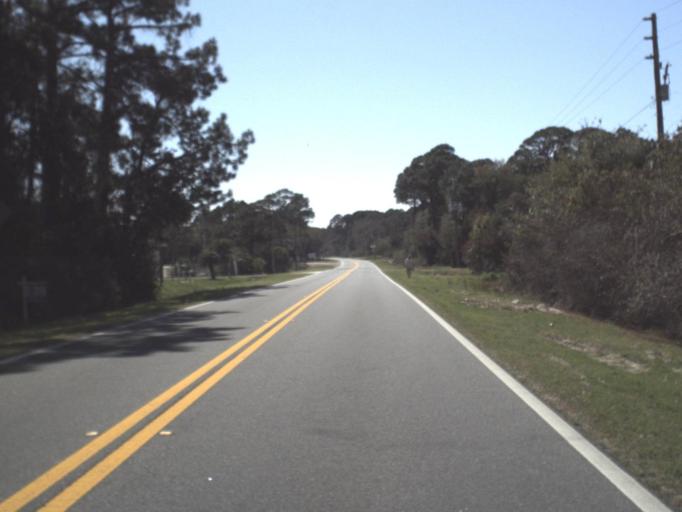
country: US
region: Florida
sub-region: Franklin County
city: Carrabelle
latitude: 29.8818
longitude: -84.5939
